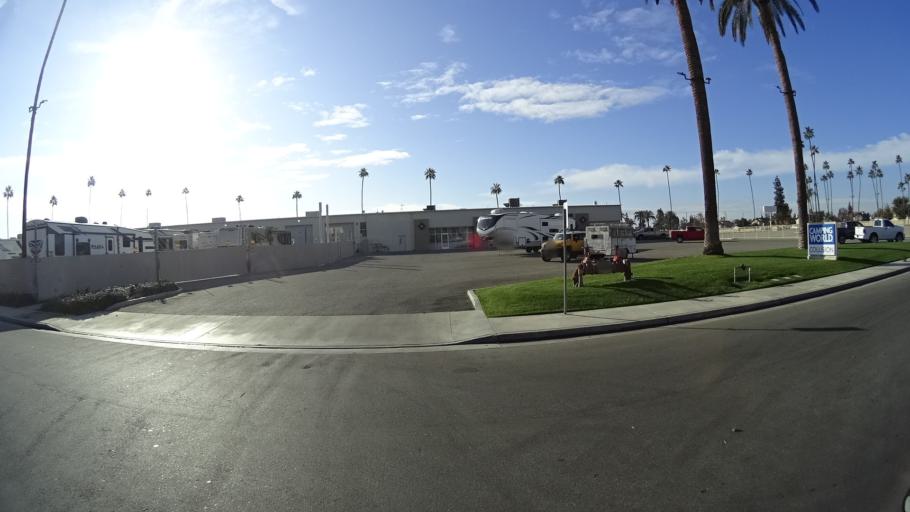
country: US
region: California
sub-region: Kern County
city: Greenfield
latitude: 35.3032
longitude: -119.0373
